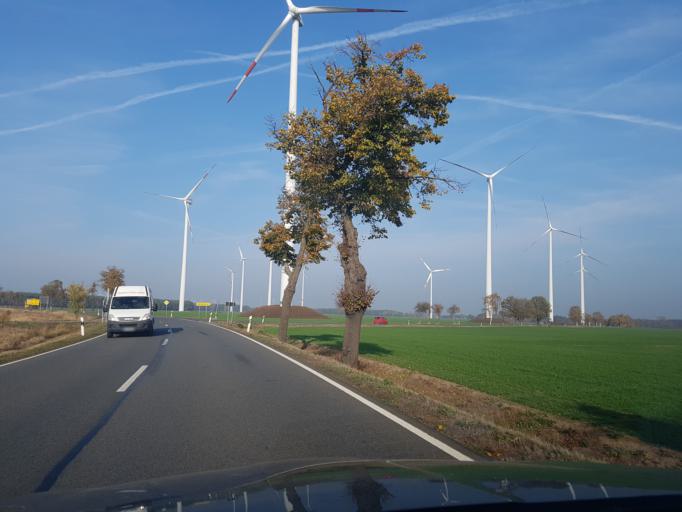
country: DE
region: Brandenburg
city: Bad Liebenwerda
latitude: 51.5222
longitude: 13.3383
